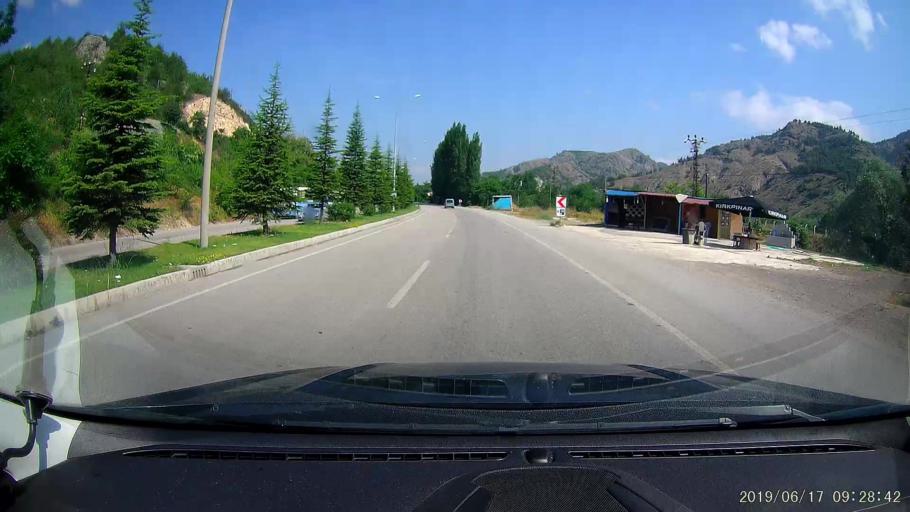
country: TR
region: Amasya
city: Amasya
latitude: 40.6912
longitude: 35.8211
